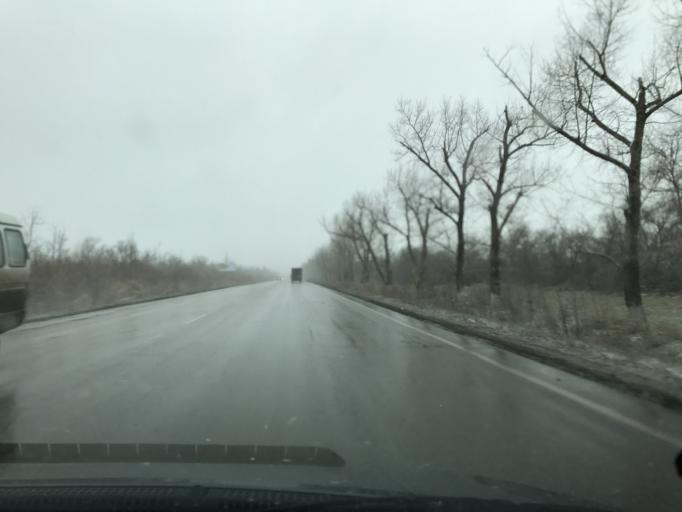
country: RU
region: Rostov
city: Bataysk
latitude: 47.0619
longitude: 39.8140
